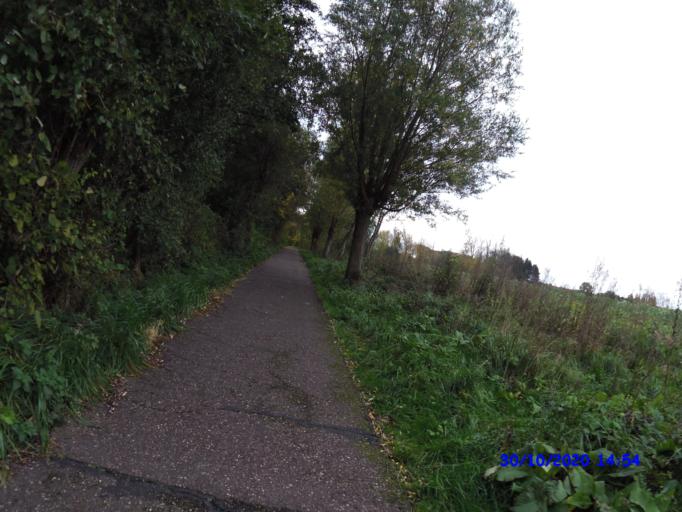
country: BE
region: Flanders
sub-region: Provincie Vlaams-Brabant
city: Landen
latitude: 50.7657
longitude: 5.0829
